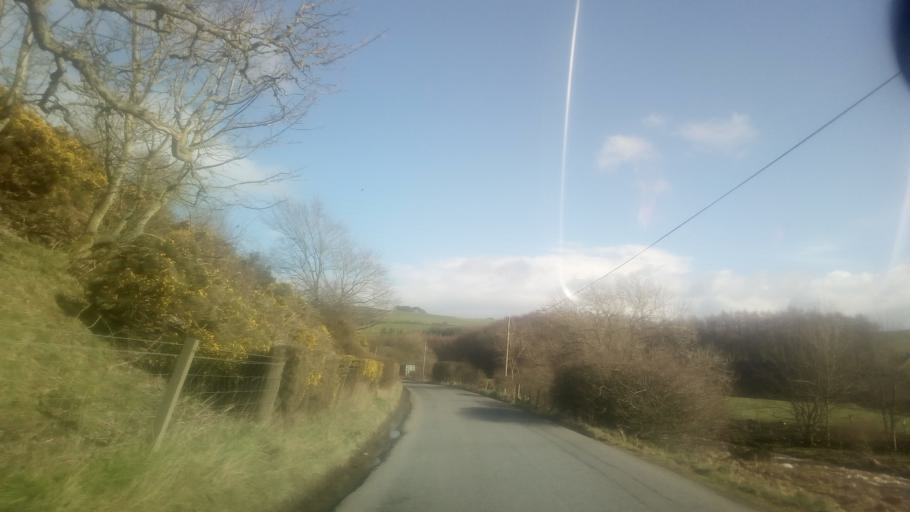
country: GB
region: Scotland
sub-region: The Scottish Borders
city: Hawick
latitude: 55.4112
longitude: -2.8384
